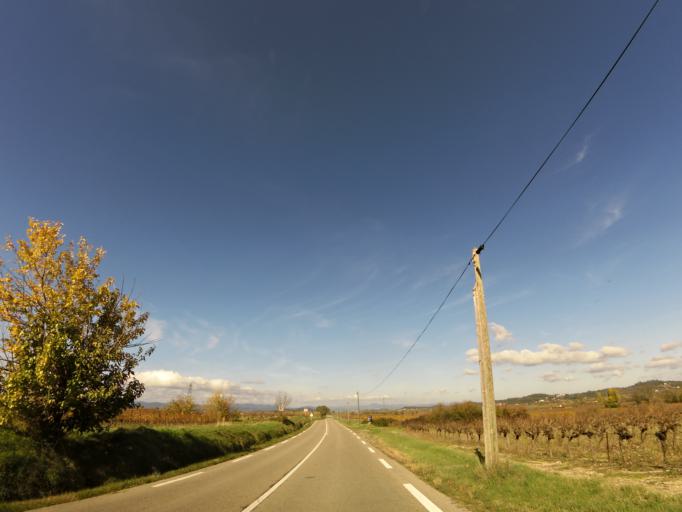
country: FR
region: Languedoc-Roussillon
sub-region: Departement du Gard
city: Ledignan
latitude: 43.9984
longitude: 4.1046
